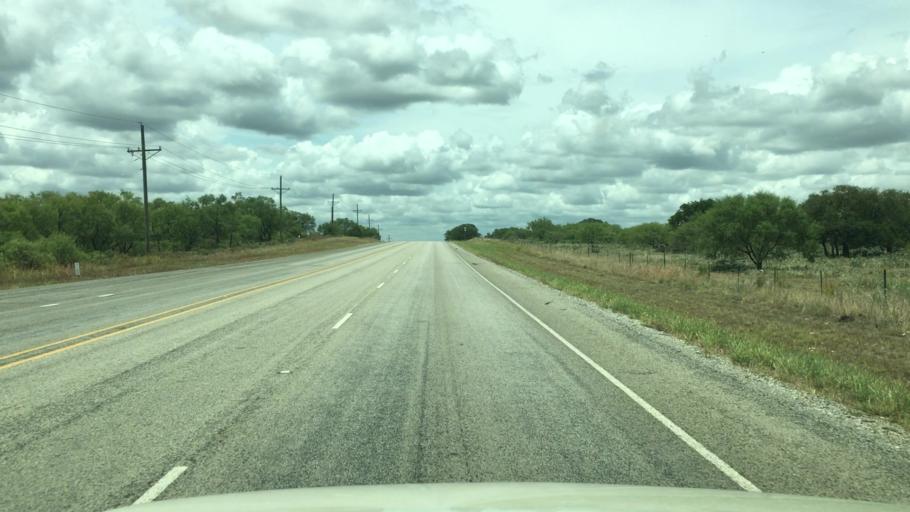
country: US
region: Texas
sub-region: McCulloch County
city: Brady
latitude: 31.0024
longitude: -99.1786
